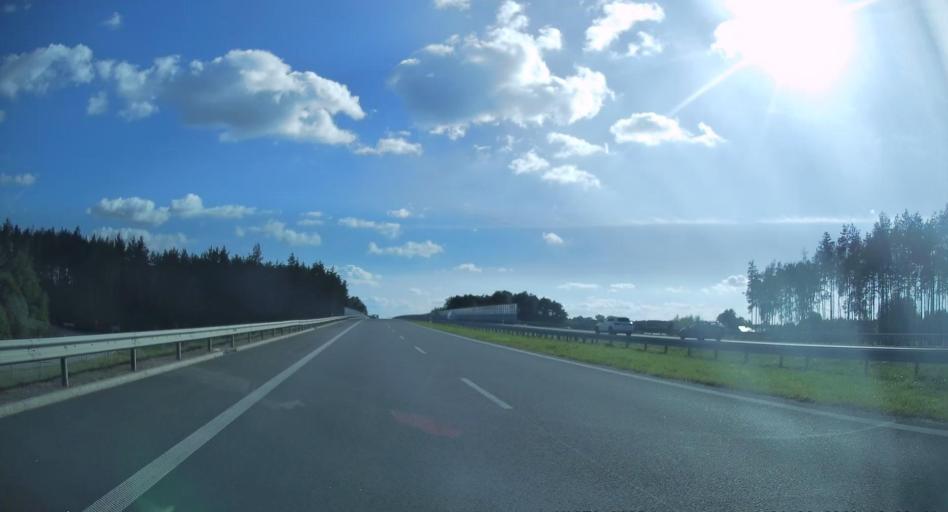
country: PL
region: Masovian Voivodeship
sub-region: Powiat szydlowiecki
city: Oronsko
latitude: 51.3128
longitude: 21.0124
